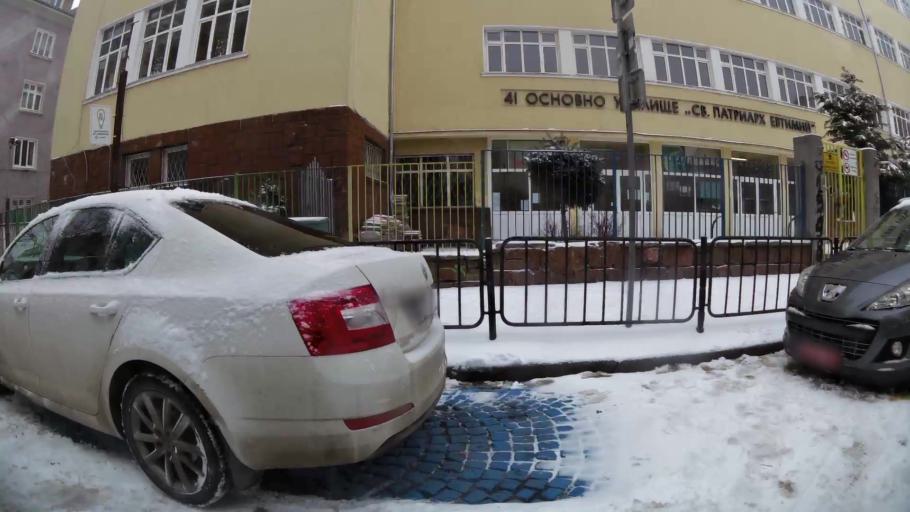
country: BG
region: Sofia-Capital
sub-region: Stolichna Obshtina
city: Sofia
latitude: 42.6926
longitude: 23.3165
